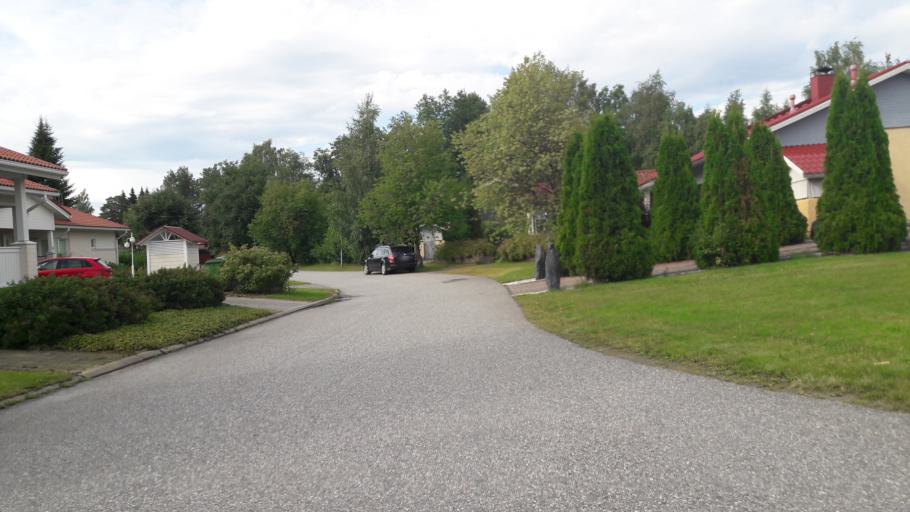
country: FI
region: North Karelia
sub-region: Joensuu
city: Joensuu
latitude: 62.5838
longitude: 29.8073
